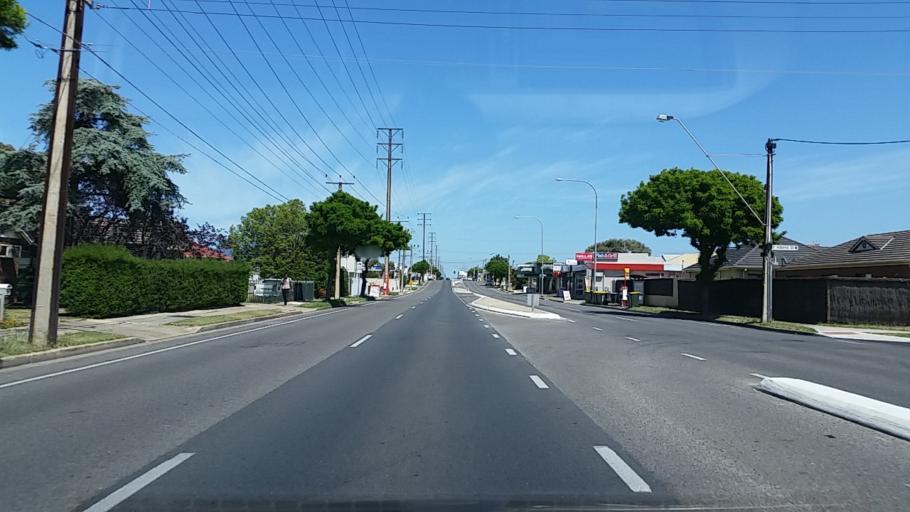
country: AU
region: South Australia
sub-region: Charles Sturt
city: Findon
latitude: -34.9058
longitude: 138.5267
